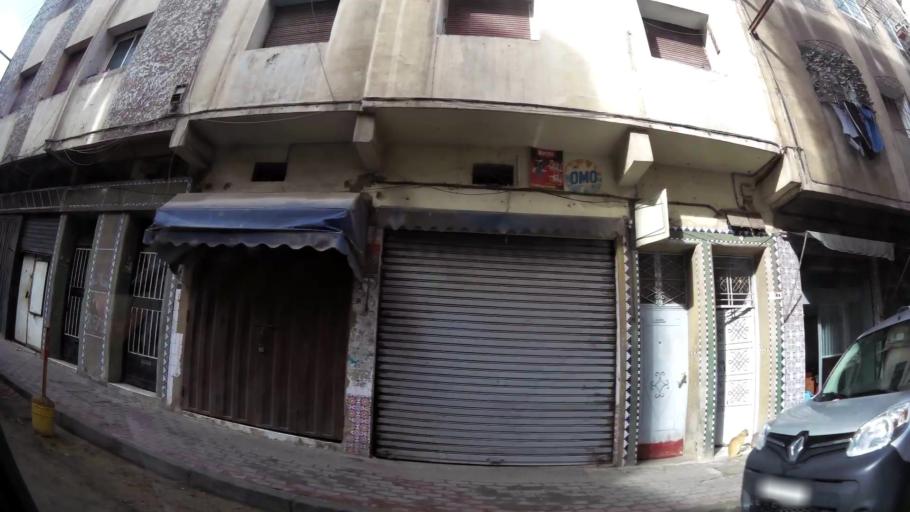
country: MA
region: Grand Casablanca
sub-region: Casablanca
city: Casablanca
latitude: 33.5701
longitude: -7.5801
